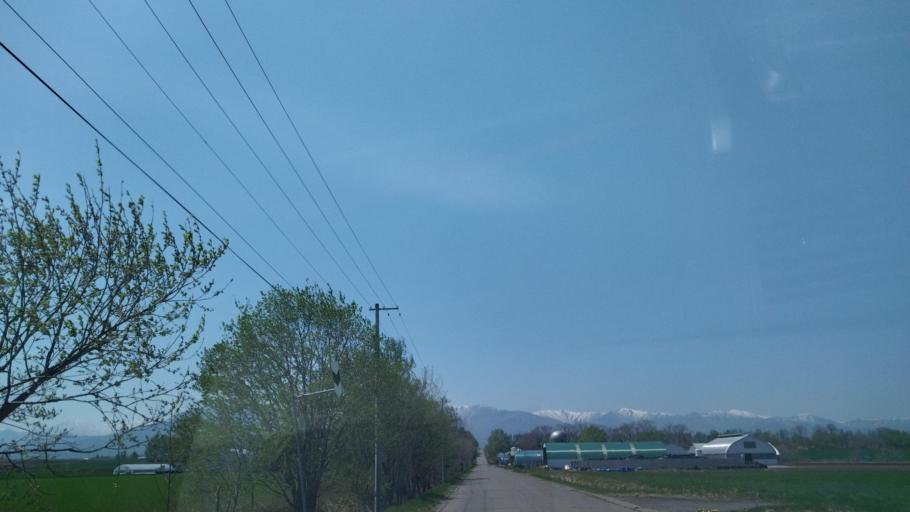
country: JP
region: Hokkaido
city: Obihiro
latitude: 42.8940
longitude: 143.0245
